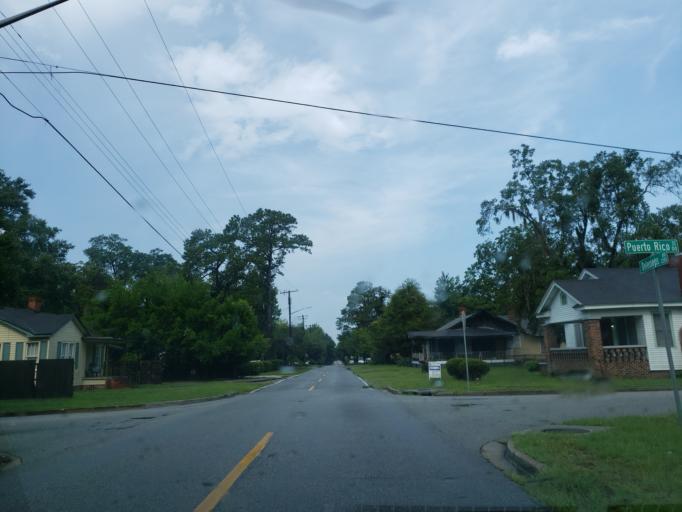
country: US
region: Georgia
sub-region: Chatham County
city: Thunderbolt
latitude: 32.0325
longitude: -81.0747
